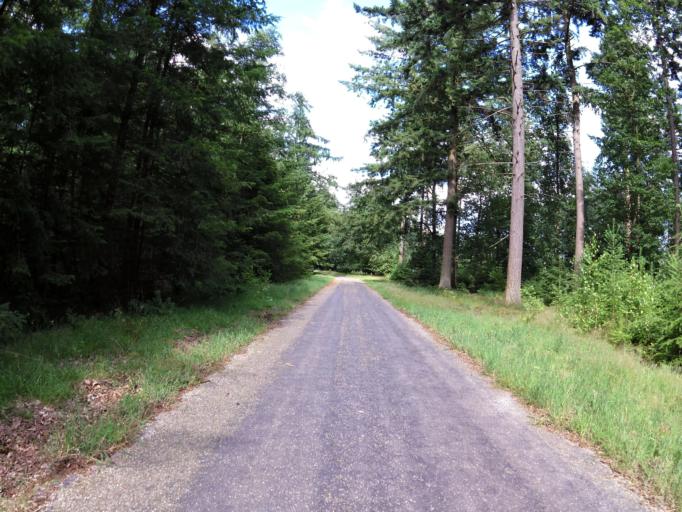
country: NL
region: North Brabant
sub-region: Gemeente Valkenswaard
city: Valkenswaard
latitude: 51.3490
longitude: 5.5155
